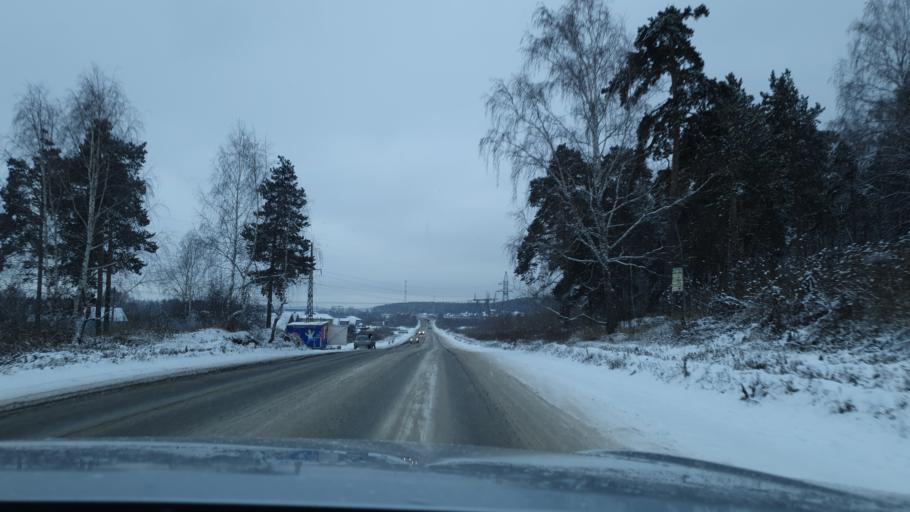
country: RU
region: Sverdlovsk
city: Istok
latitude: 56.7773
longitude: 60.7395
